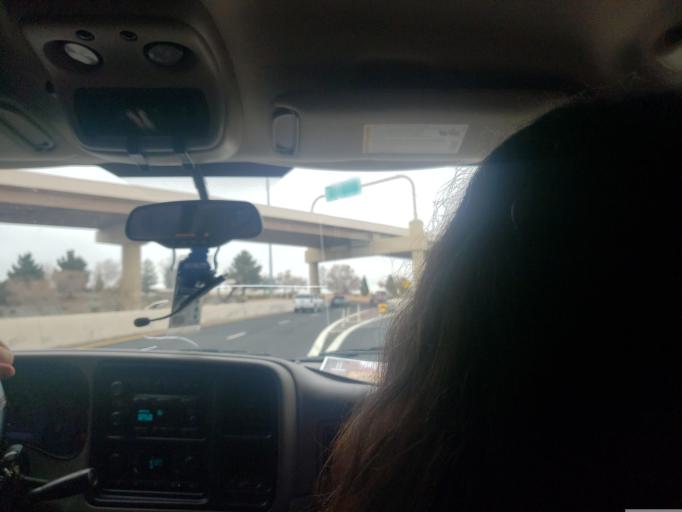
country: US
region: New Mexico
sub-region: Bernalillo County
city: Albuquerque
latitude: 35.1079
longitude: -106.7026
